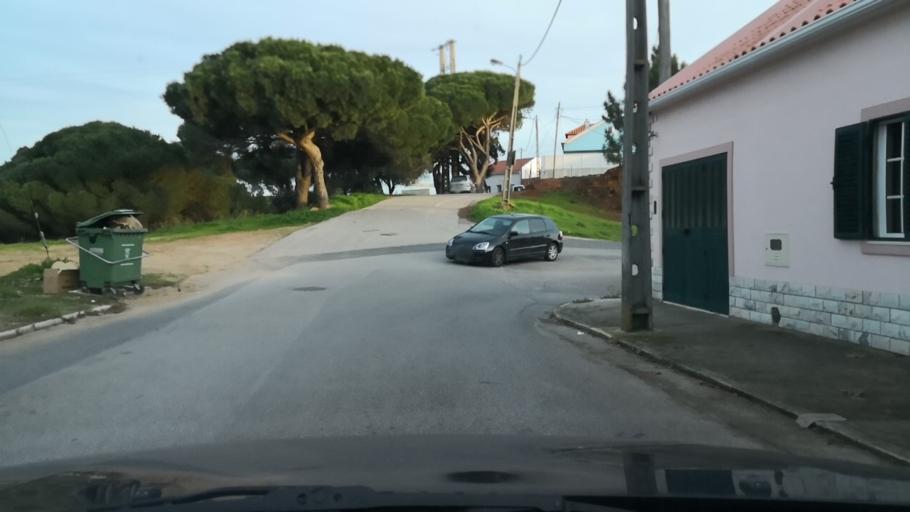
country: PT
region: Setubal
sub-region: Setubal
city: Setubal
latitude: 38.5270
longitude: -8.8616
